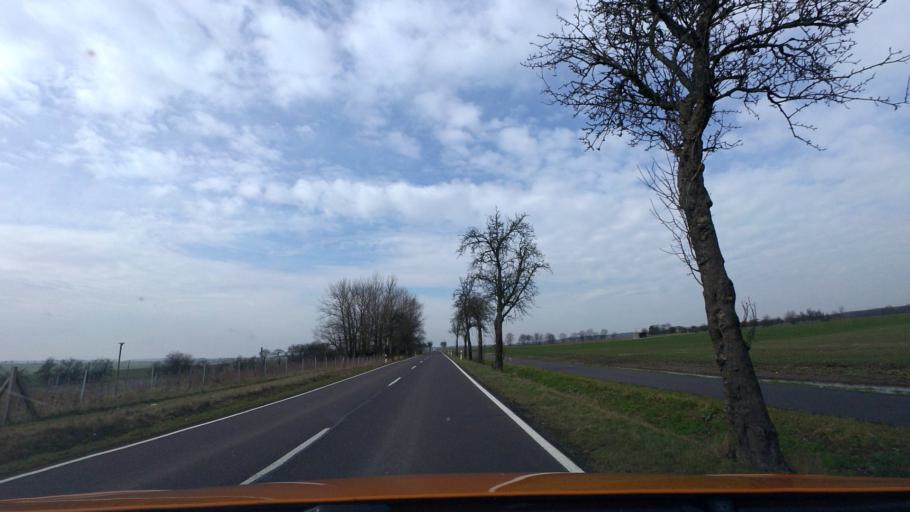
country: DE
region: Saxony-Anhalt
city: Erxleben
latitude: 52.2203
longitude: 11.2272
